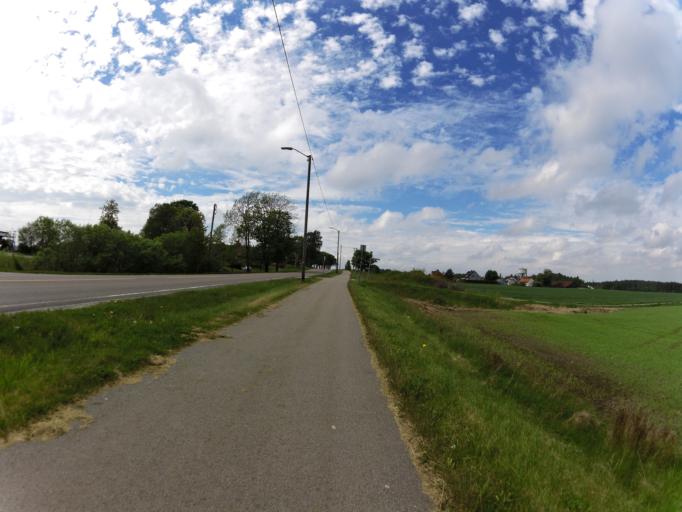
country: NO
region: Ostfold
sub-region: Rade
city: Karlshus
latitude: 59.3458
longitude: 10.8991
